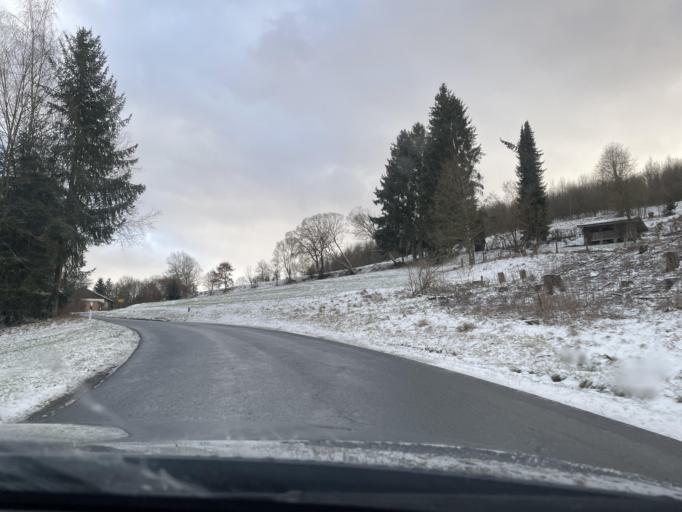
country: DE
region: Bavaria
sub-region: Lower Bavaria
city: Viechtach
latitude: 49.0905
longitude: 12.8770
